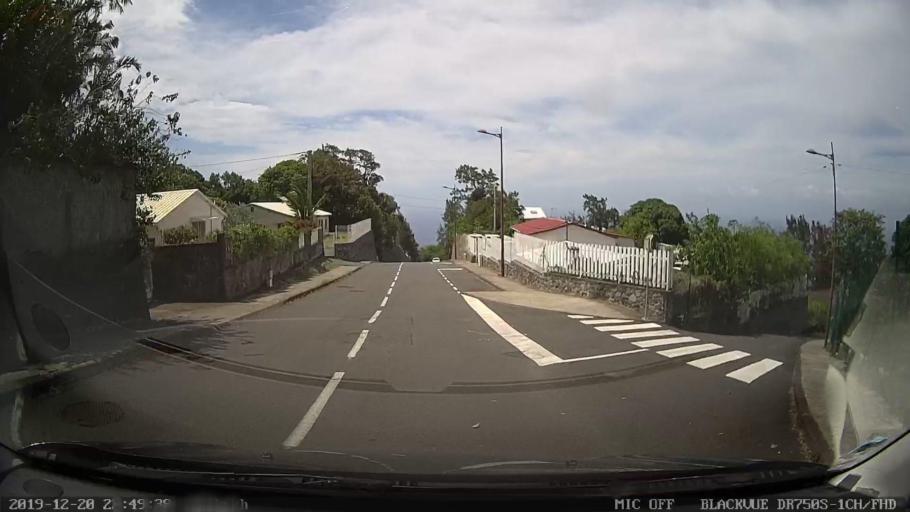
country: RE
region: Reunion
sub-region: Reunion
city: Saint-Denis
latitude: -20.8882
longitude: 55.4226
